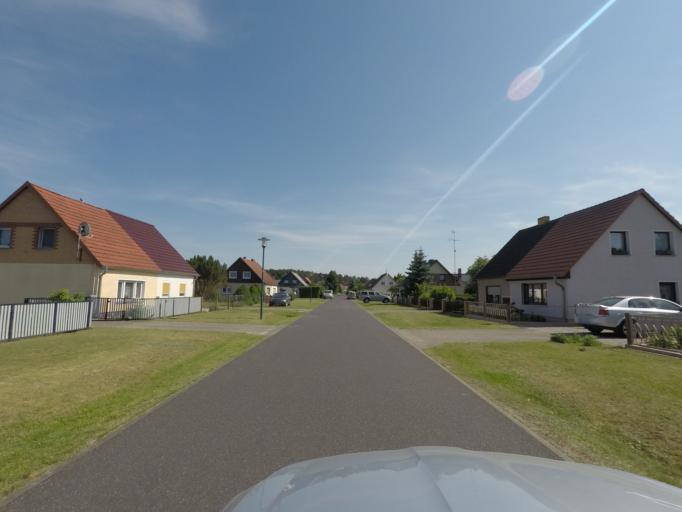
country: DE
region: Brandenburg
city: Melchow
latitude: 52.8633
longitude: 13.7232
